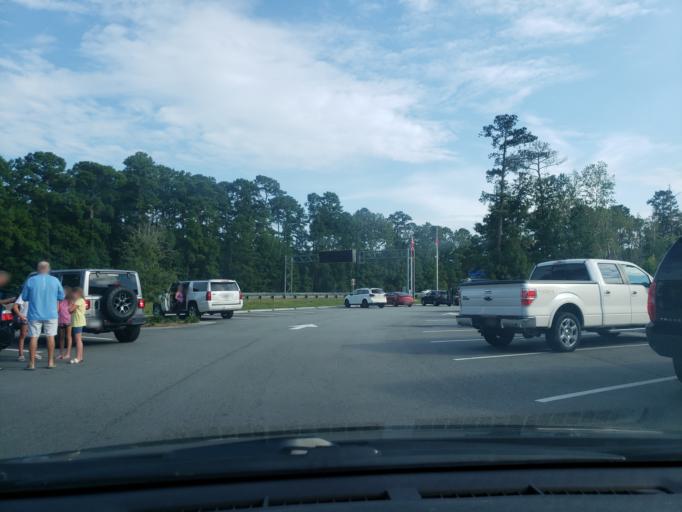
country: US
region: Georgia
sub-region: Chatham County
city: Port Wentworth
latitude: 32.2171
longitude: -81.1742
